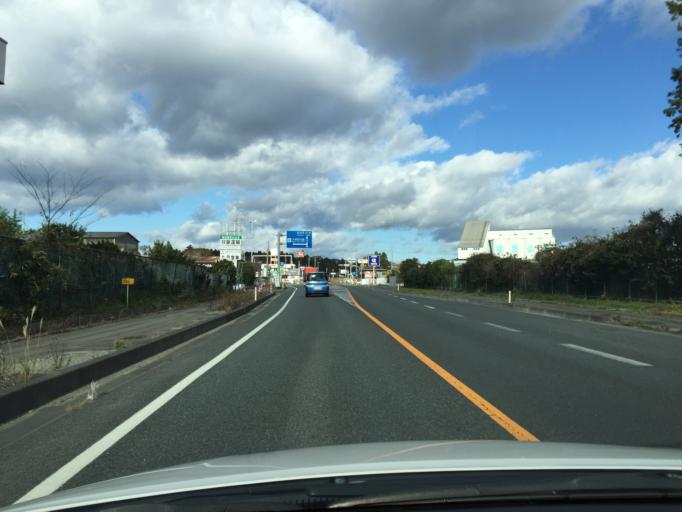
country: JP
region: Fukushima
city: Namie
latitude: 37.4028
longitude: 140.9996
